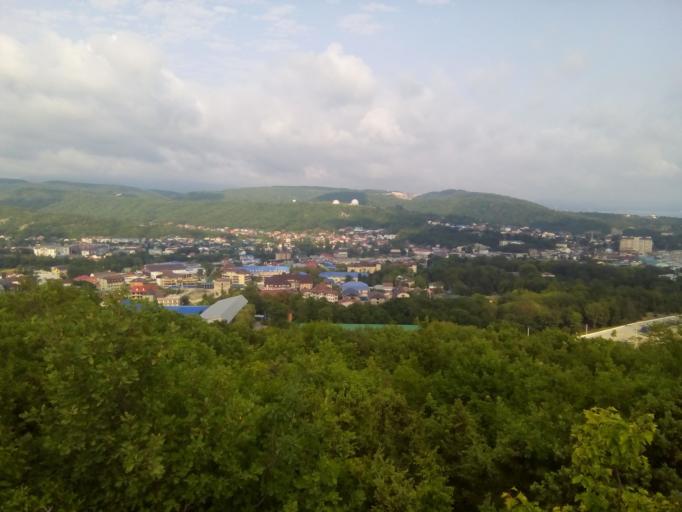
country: RU
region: Krasnodarskiy
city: Dzhubga
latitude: 44.3162
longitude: 38.6882
